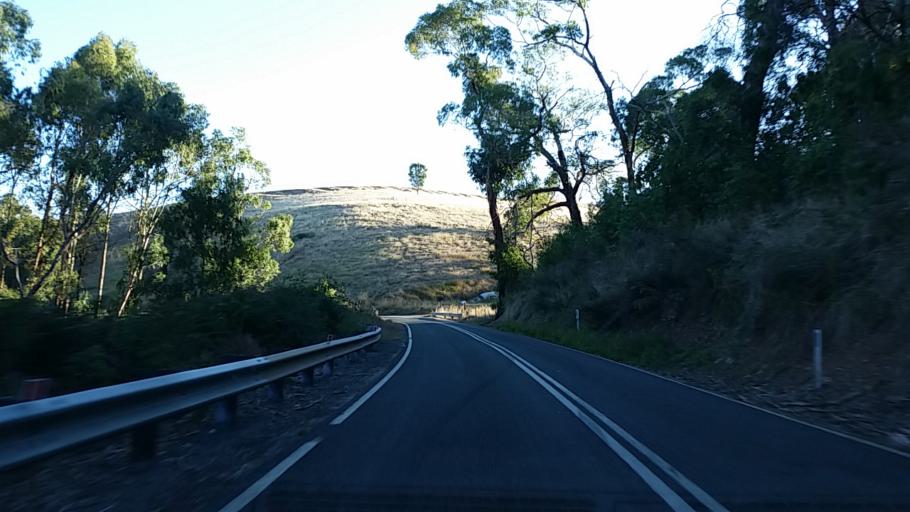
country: AU
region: South Australia
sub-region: Adelaide Hills
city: Gumeracha
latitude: -34.8245
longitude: 138.8515
